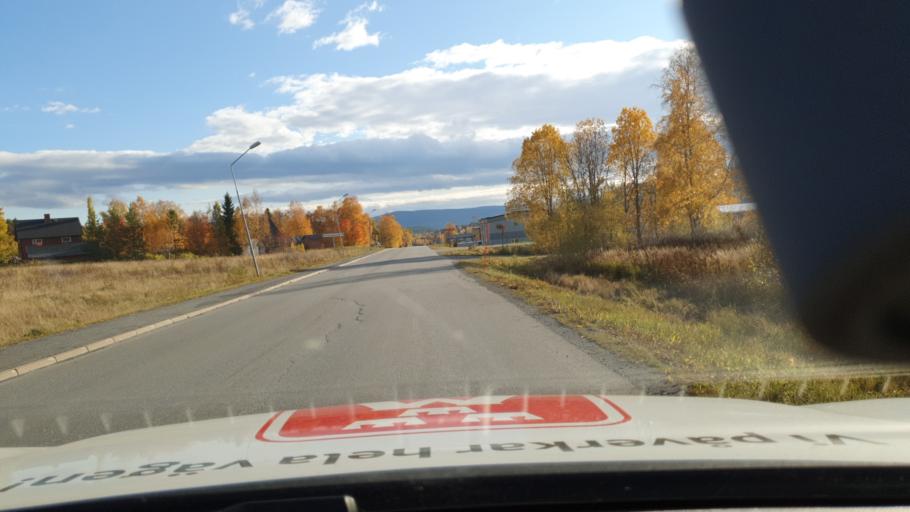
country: SE
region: Jaemtland
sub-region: Are Kommun
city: Jarpen
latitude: 63.3618
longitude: 13.4389
